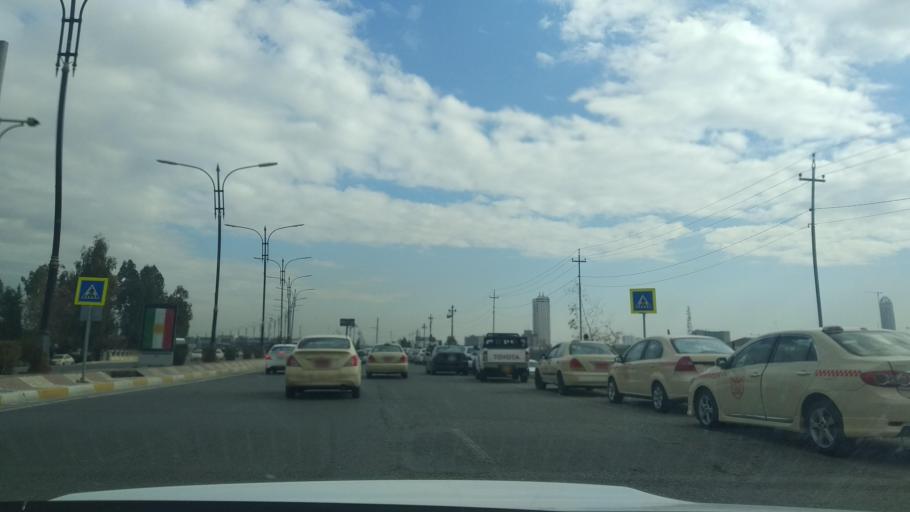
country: IQ
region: Arbil
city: Erbil
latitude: 36.1838
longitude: 43.9819
